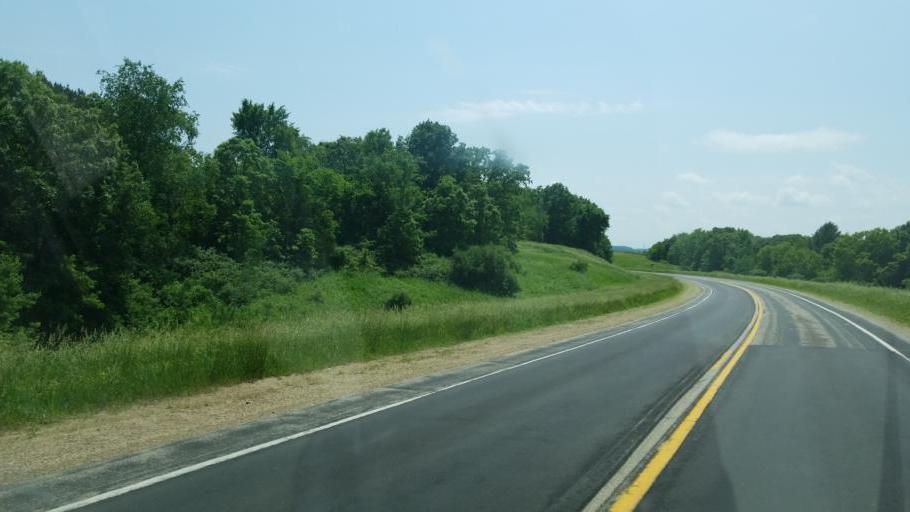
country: US
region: Wisconsin
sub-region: Monroe County
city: Cashton
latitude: 43.6042
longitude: -90.6246
